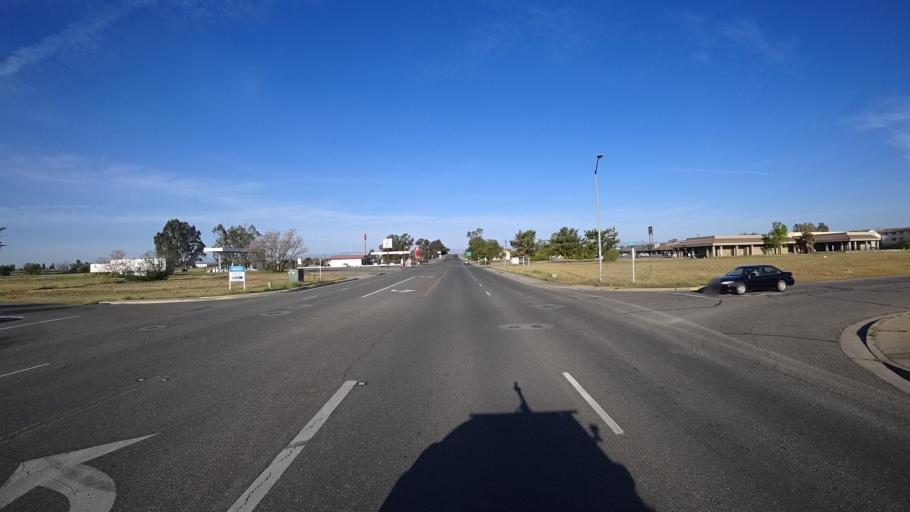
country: US
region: California
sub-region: Glenn County
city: Orland
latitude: 39.7403
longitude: -122.2015
